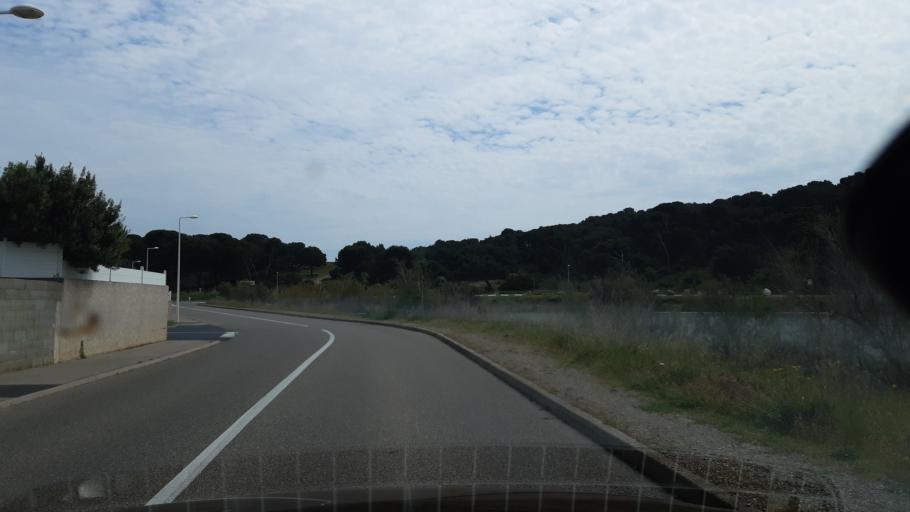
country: FR
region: Languedoc-Roussillon
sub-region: Departement de l'Aude
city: Gruissan
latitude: 43.1149
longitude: 3.0969
